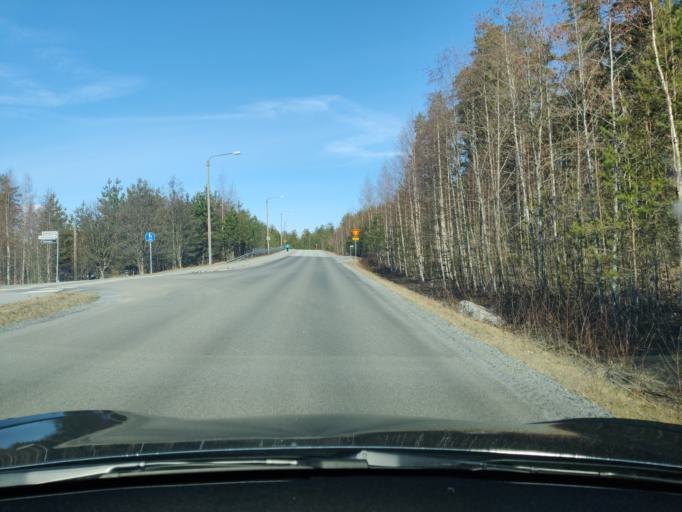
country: FI
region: Northern Savo
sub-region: Kuopio
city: Vehmersalmi
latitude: 62.7691
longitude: 28.0101
